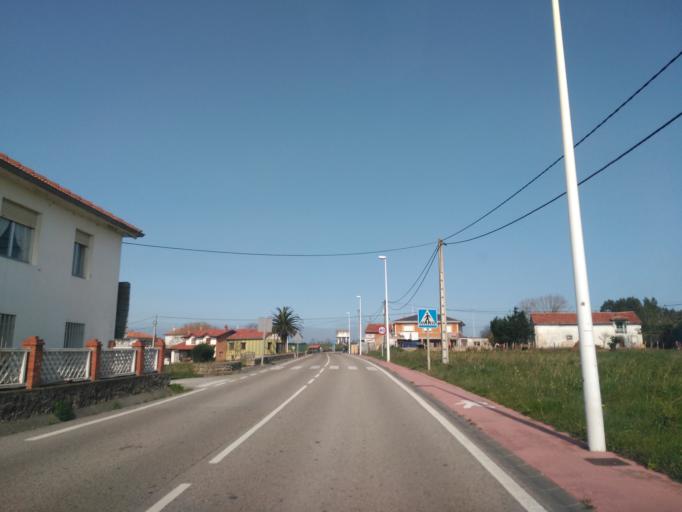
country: ES
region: Cantabria
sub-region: Provincia de Cantabria
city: Suances
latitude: 43.4192
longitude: -4.0687
